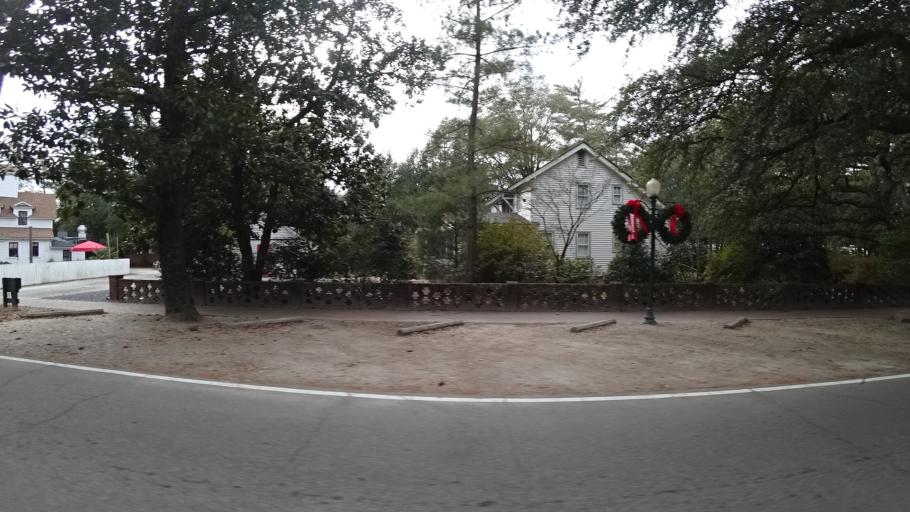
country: US
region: North Carolina
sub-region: Moore County
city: Pinehurst
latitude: 35.1955
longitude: -79.4708
